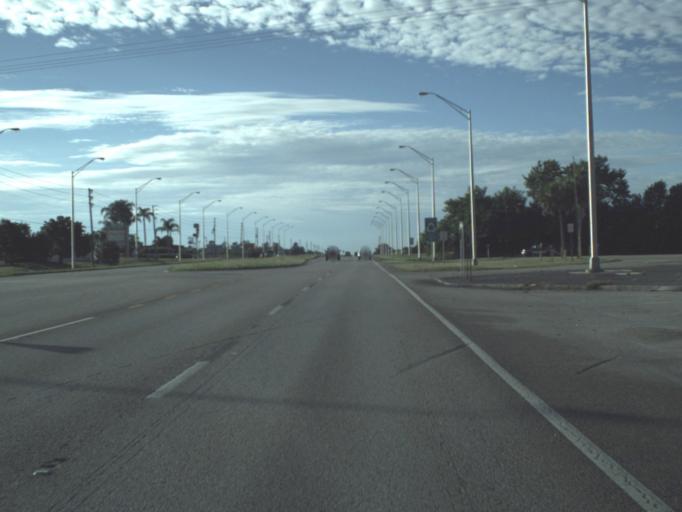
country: US
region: Florida
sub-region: Highlands County
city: Lake Placid
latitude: 27.2673
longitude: -81.3481
